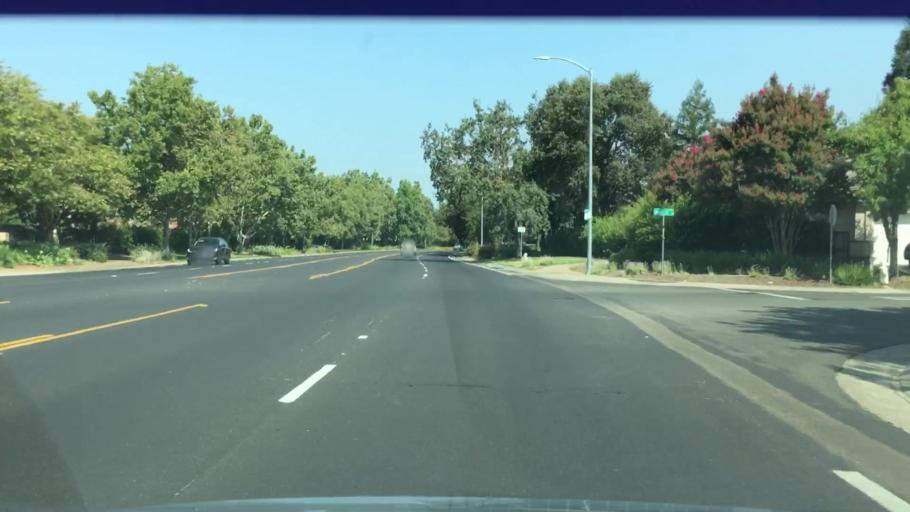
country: US
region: California
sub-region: Sacramento County
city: Laguna
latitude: 38.4115
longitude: -121.4056
